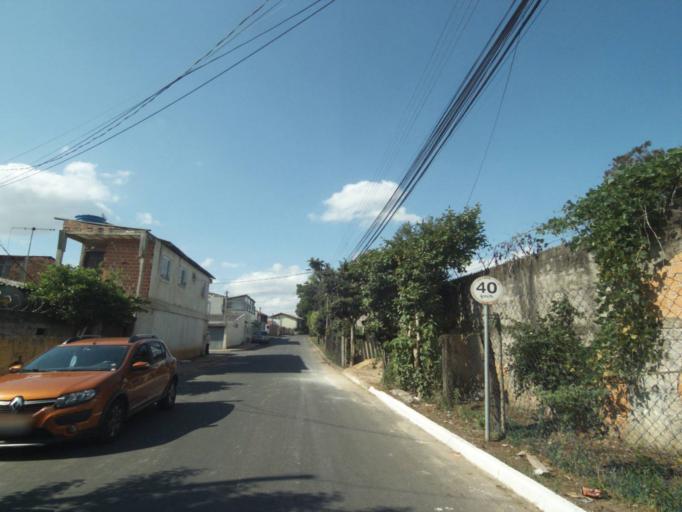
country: BR
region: Parana
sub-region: Curitiba
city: Curitiba
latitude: -25.4917
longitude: -49.3212
